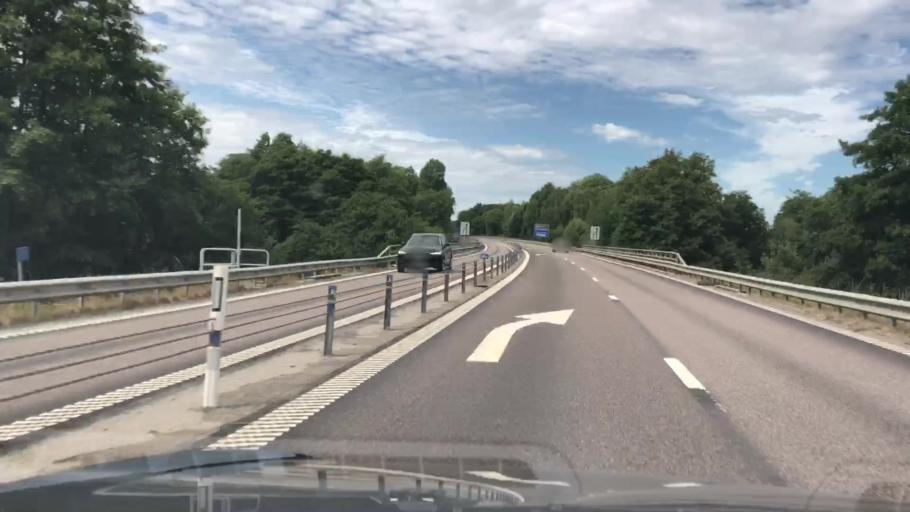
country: SE
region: Blekinge
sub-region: Karlskrona Kommun
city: Rodeby
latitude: 56.2023
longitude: 15.6688
